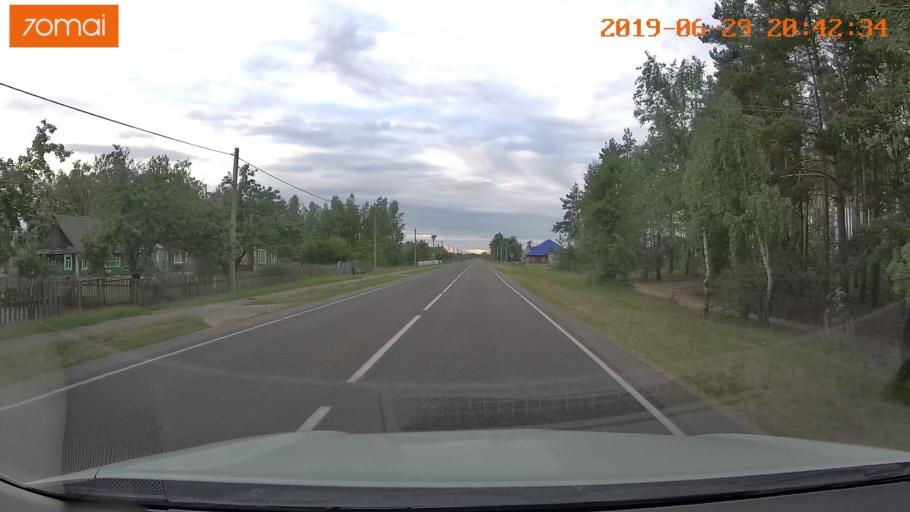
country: BY
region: Brest
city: Hantsavichy
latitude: 52.5988
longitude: 26.3243
